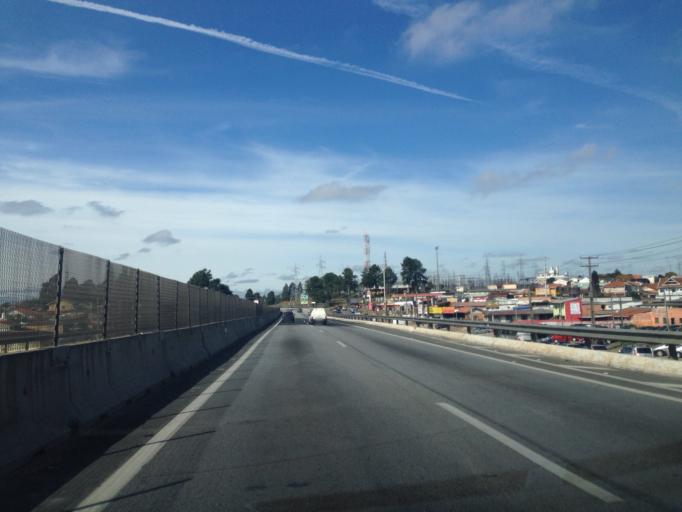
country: BR
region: Parana
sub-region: Pinhais
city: Pinhais
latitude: -25.4722
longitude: -49.2108
